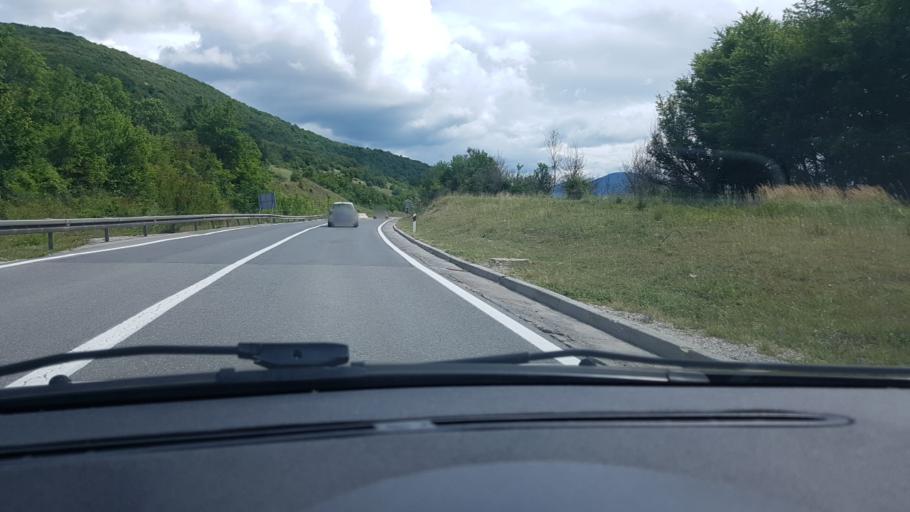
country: HR
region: Zadarska
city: Gracac
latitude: 44.5014
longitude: 15.7631
